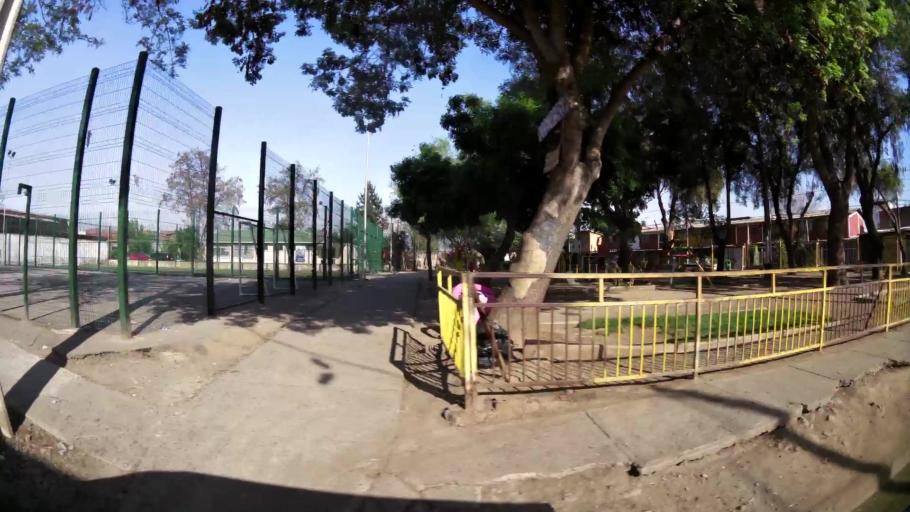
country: CL
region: Santiago Metropolitan
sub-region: Provincia de Santiago
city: Lo Prado
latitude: -33.4161
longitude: -70.7674
